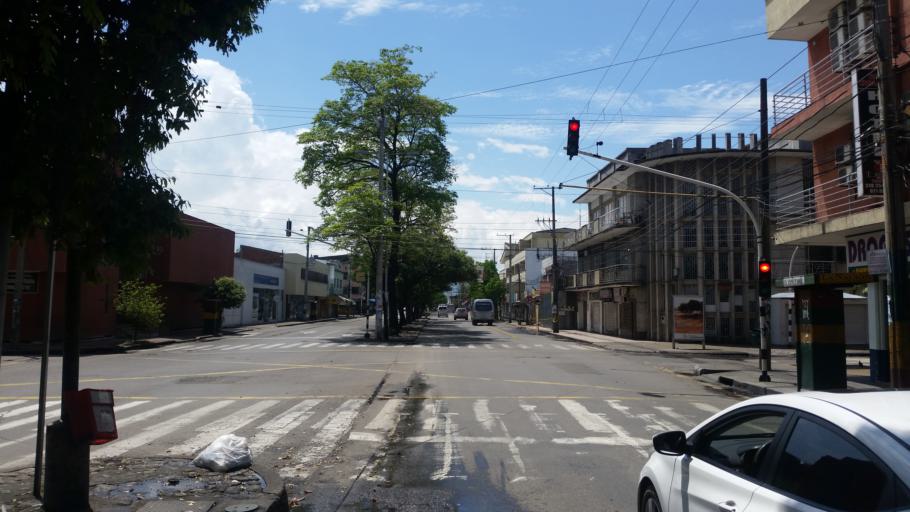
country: CO
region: Huila
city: Neiva
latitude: 2.9271
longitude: -75.2866
